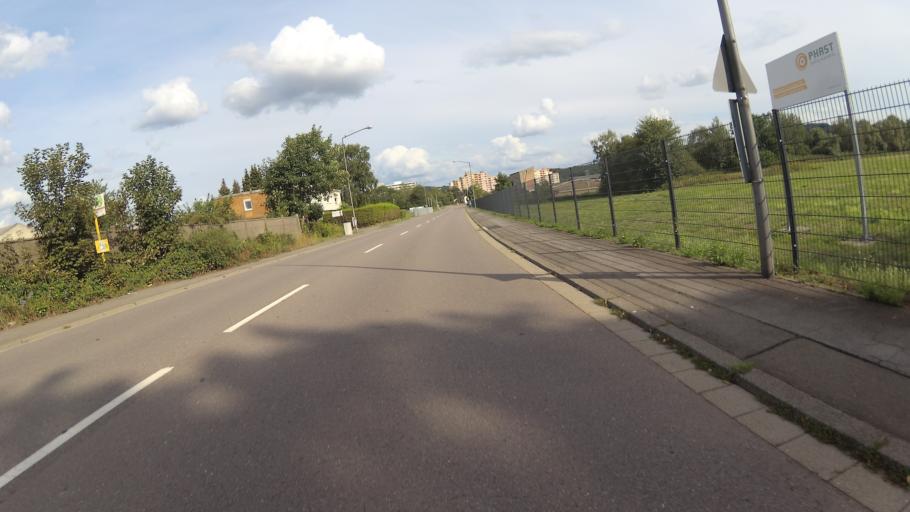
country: DE
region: Saarland
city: Homburg
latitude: 49.3140
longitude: 7.3266
